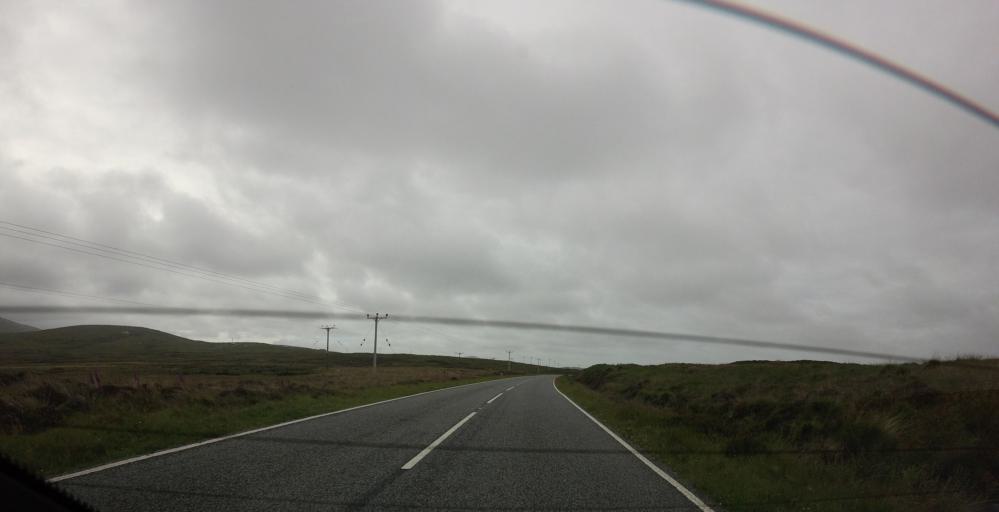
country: GB
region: Scotland
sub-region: Eilean Siar
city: Isle of South Uist
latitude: 57.2730
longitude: -7.3654
